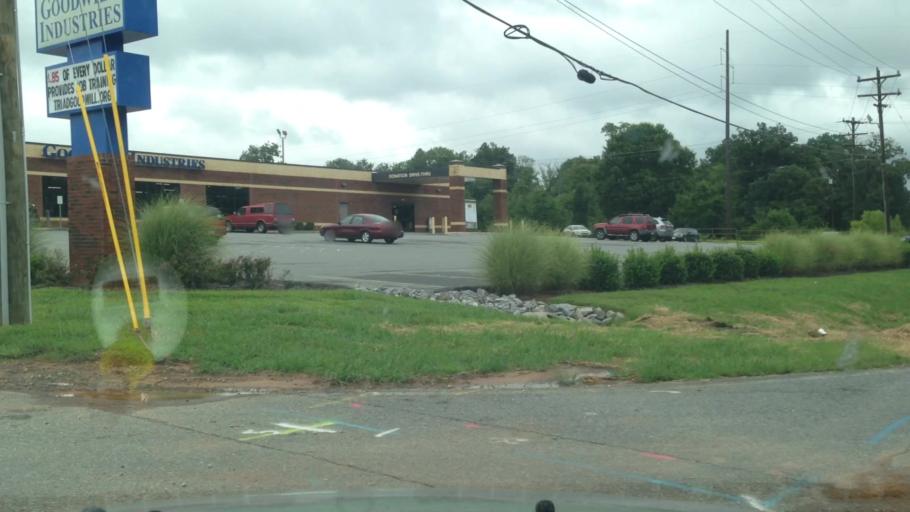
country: US
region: North Carolina
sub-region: Rockingham County
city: Mayodan
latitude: 36.4175
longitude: -79.9330
